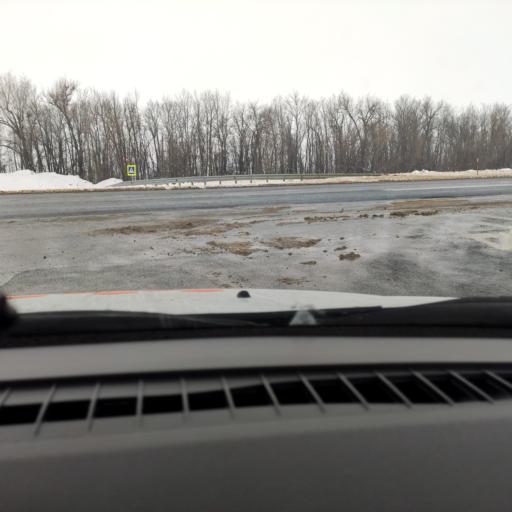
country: RU
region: Samara
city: Mayskoye
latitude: 52.4518
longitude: 50.5173
